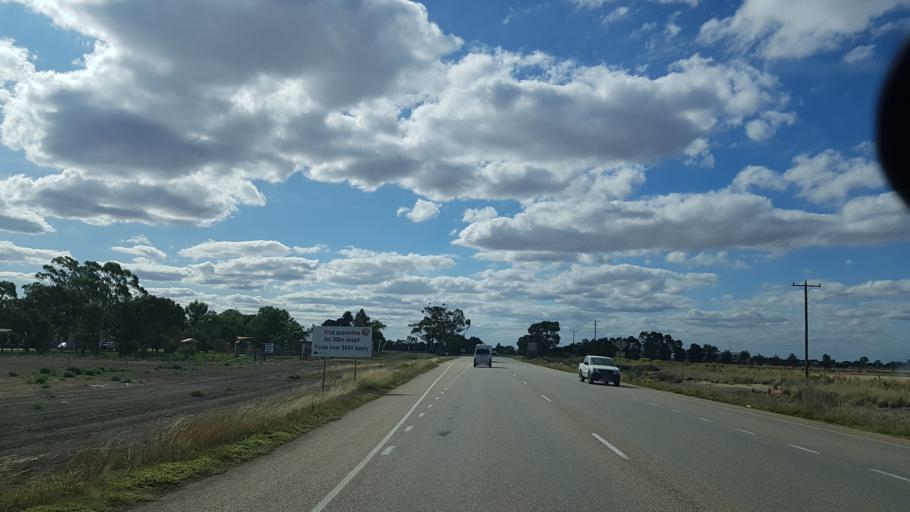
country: AU
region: Victoria
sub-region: Swan Hill
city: Swan Hill
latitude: -35.7618
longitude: 143.9305
